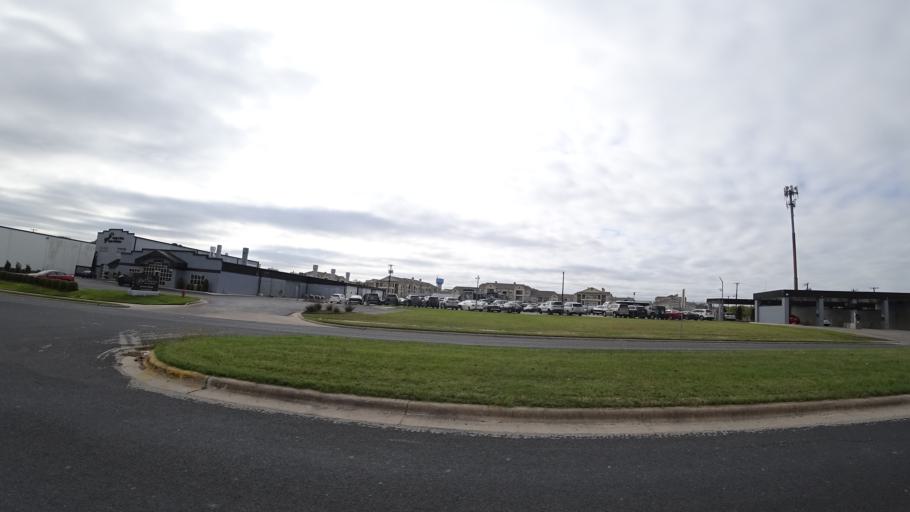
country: US
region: Texas
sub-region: Travis County
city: Windemere
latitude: 30.4563
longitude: -97.6535
